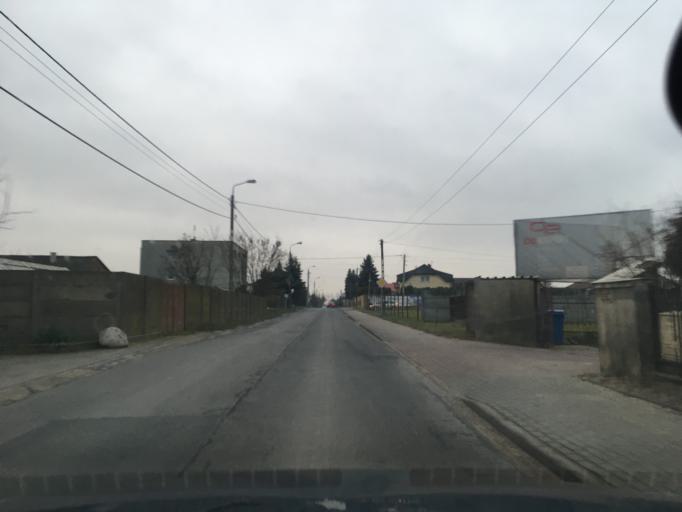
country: PL
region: Masovian Voivodeship
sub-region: Powiat piaseczynski
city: Mysiadlo
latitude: 52.1225
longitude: 20.9795
